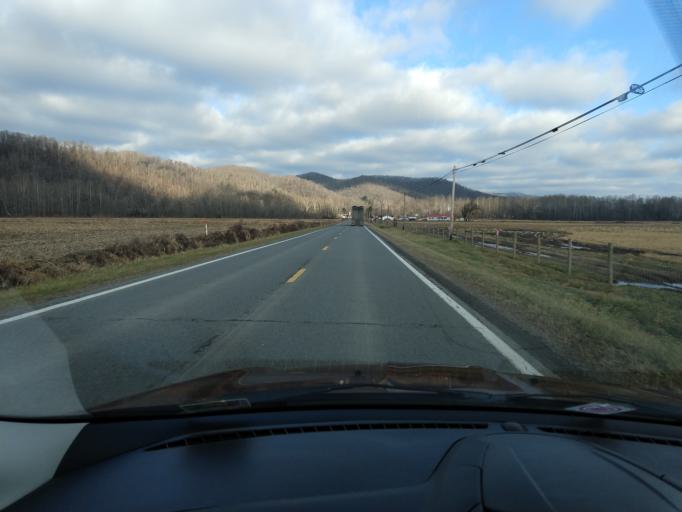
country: US
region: West Virginia
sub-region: Randolph County
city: Elkins
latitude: 38.7031
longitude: -79.9768
